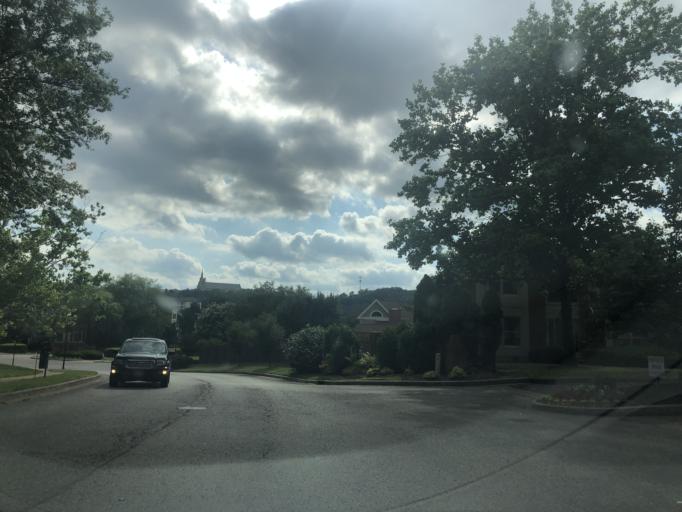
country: US
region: Tennessee
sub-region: Davidson County
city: Oak Hill
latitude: 36.0954
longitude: -86.8164
